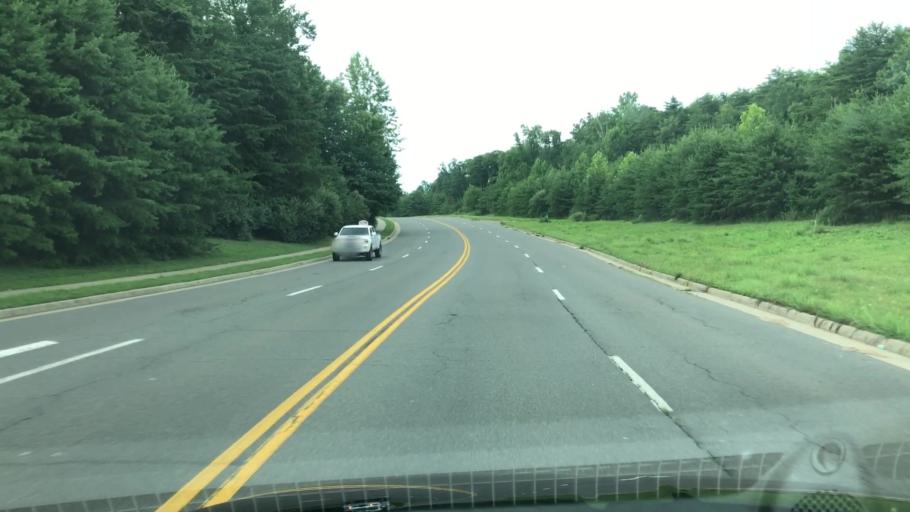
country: US
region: Virginia
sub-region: Stafford County
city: Falmouth
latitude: 38.3641
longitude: -77.5290
